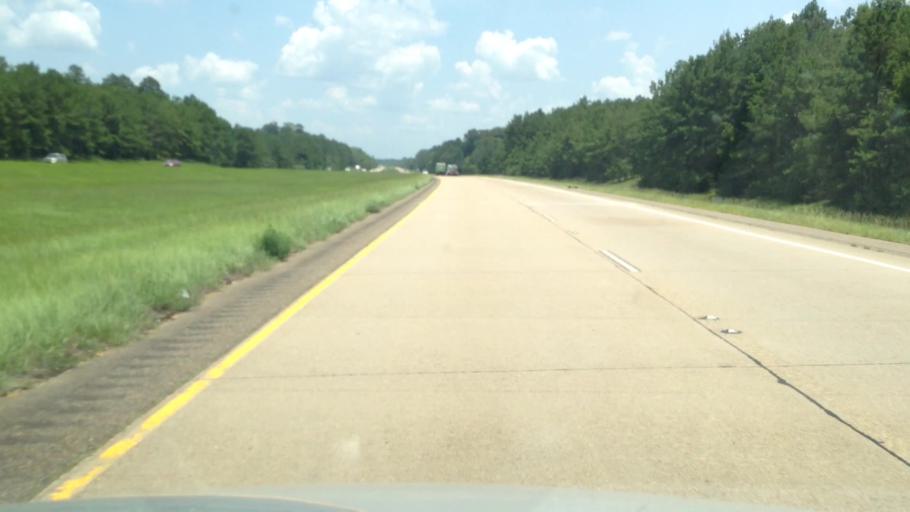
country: US
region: Louisiana
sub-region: Rapides Parish
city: Lecompte
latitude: 31.0281
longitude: -92.4050
